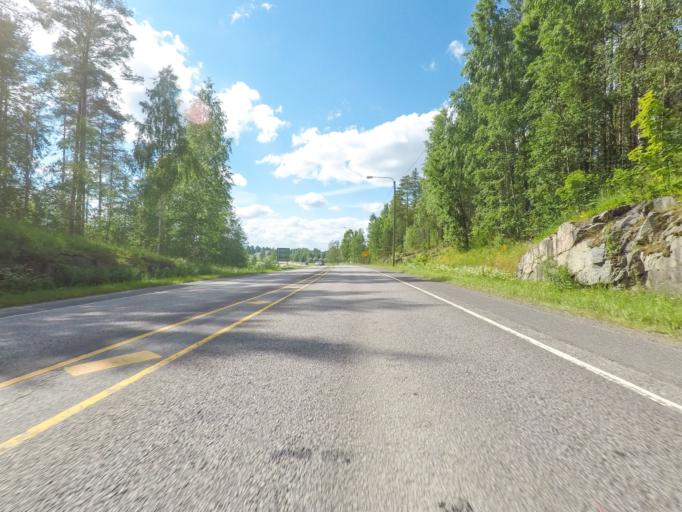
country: FI
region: Southern Savonia
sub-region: Savonlinna
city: Kerimaeki
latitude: 61.8821
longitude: 29.1059
